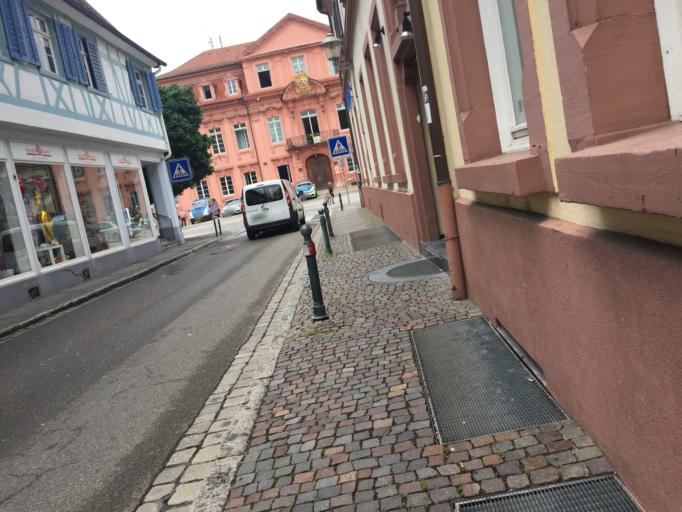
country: DE
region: Baden-Wuerttemberg
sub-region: Freiburg Region
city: Offenburg
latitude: 48.4688
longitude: 7.9435
